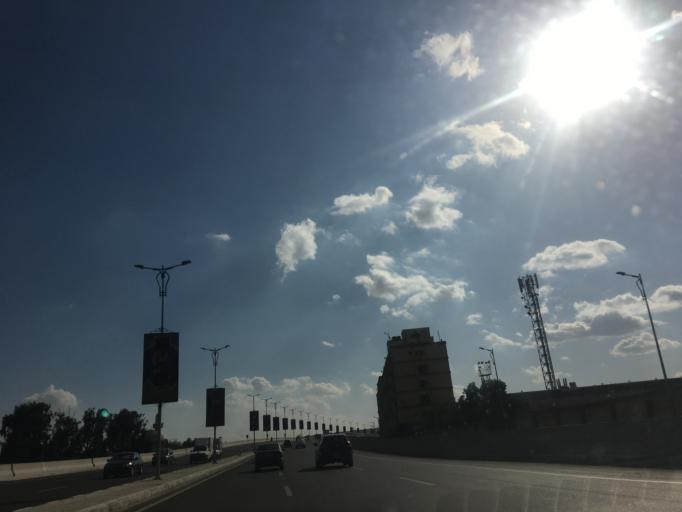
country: EG
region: Muhafazat al Qahirah
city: Cairo
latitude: 30.0462
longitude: 31.3078
